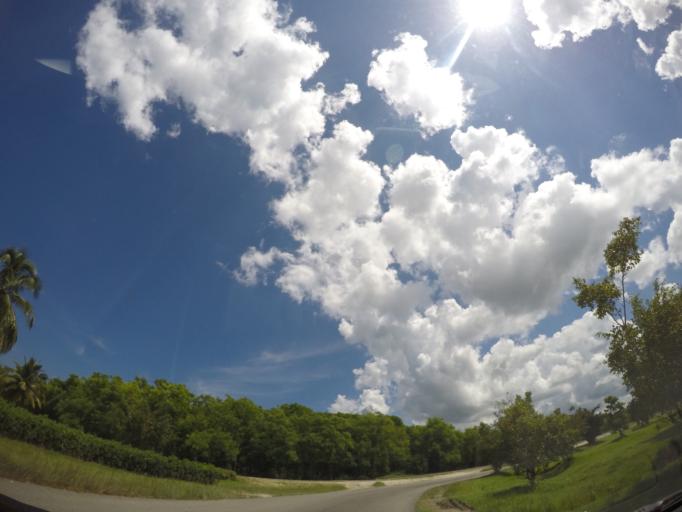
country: CU
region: La Habana
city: Havana
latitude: 23.1258
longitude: -82.4027
